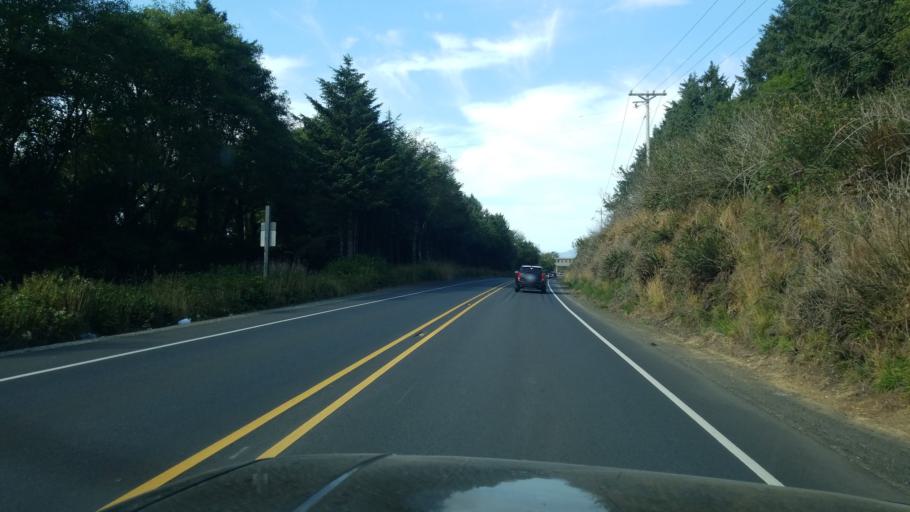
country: US
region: Oregon
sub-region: Tillamook County
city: Rockaway Beach
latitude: 45.5890
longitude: -123.9479
